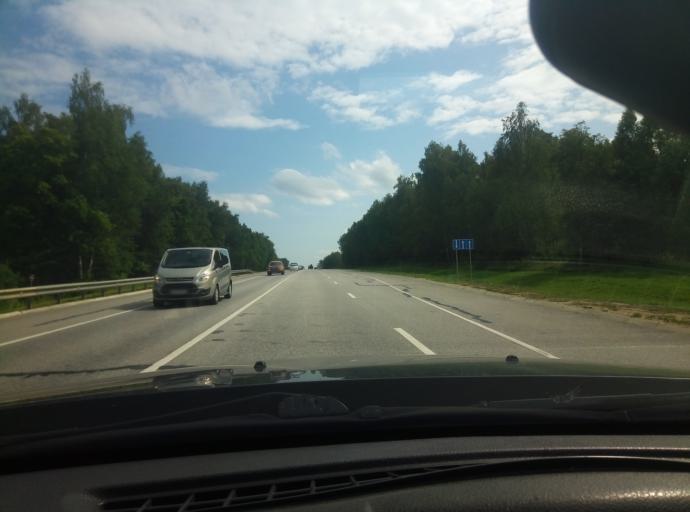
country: RU
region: Tula
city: Leninskiy
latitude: 54.3832
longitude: 37.5149
